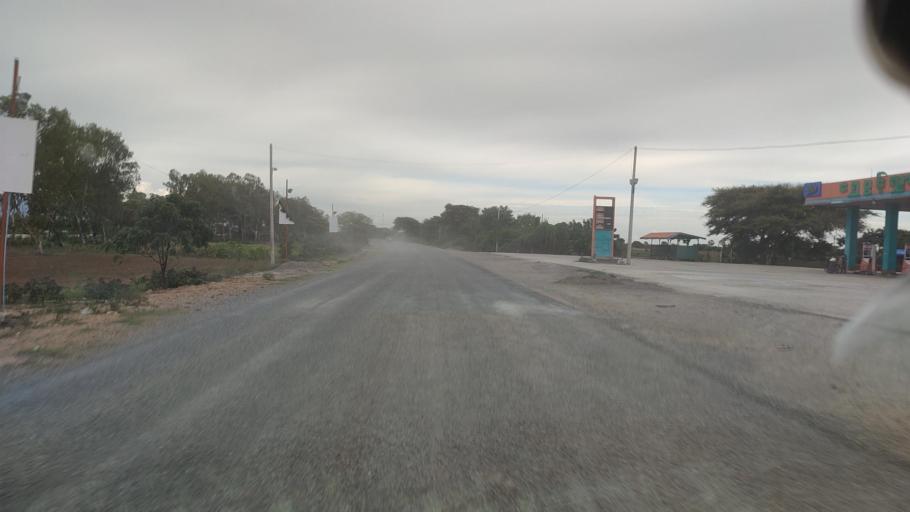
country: MM
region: Mandalay
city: Meiktila
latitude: 21.2195
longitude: 96.0213
